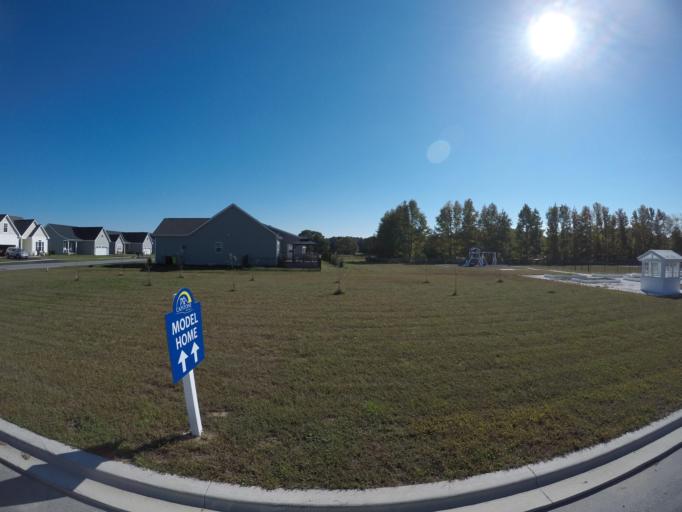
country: US
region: Delaware
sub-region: Sussex County
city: Milton
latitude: 38.7962
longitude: -75.3819
